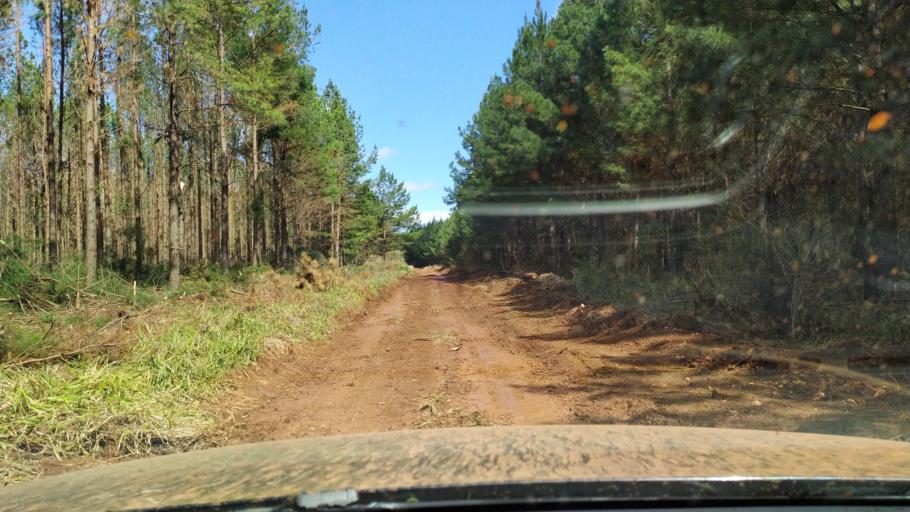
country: AR
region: Corrientes
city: Santo Tome
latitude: -28.4035
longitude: -56.0129
